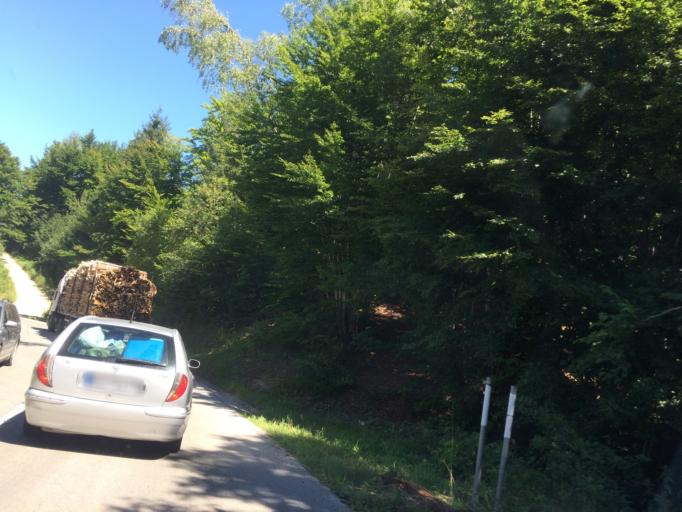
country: RS
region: Central Serbia
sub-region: Zlatiborski Okrug
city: Prijepolje
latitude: 43.3269
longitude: 19.5412
